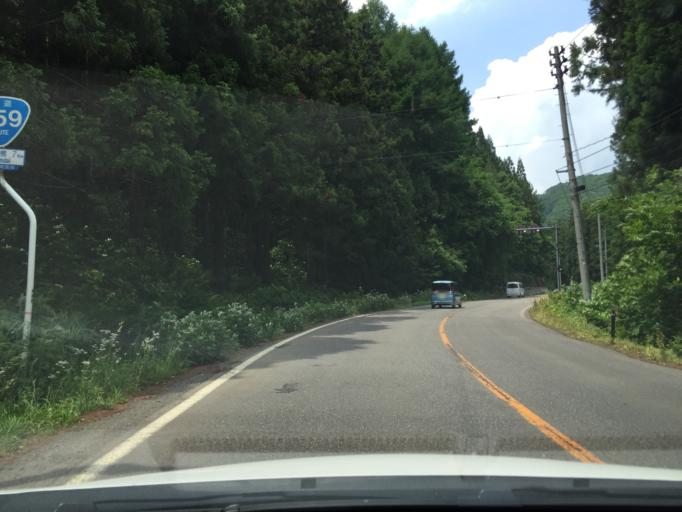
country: JP
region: Fukushima
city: Inawashiro
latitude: 37.6208
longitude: 140.1135
